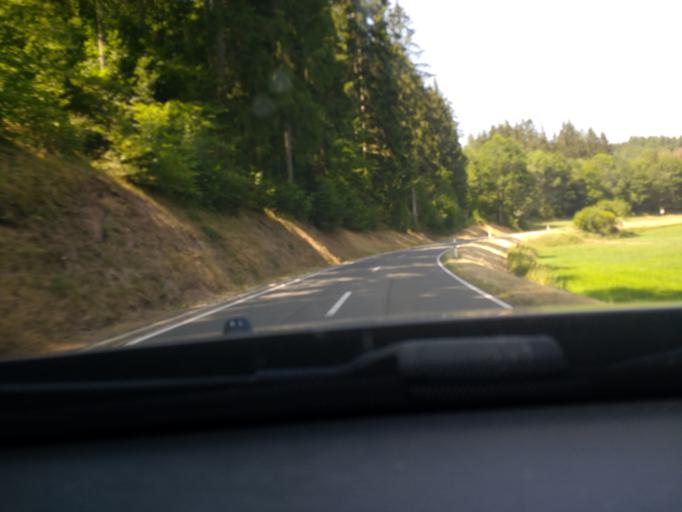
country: DE
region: Rheinland-Pfalz
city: Manderscheid
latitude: 50.0971
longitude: 6.7866
